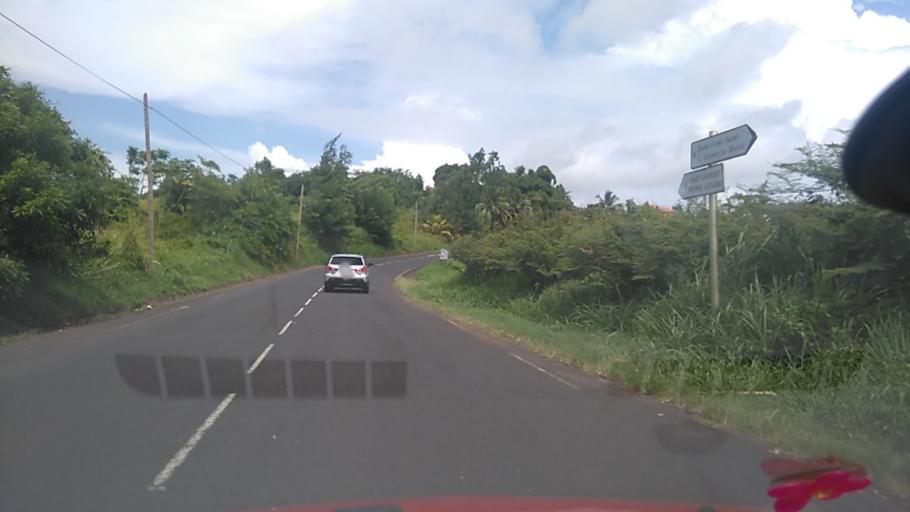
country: MQ
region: Martinique
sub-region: Martinique
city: Le Francois
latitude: 14.5932
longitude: -60.9209
